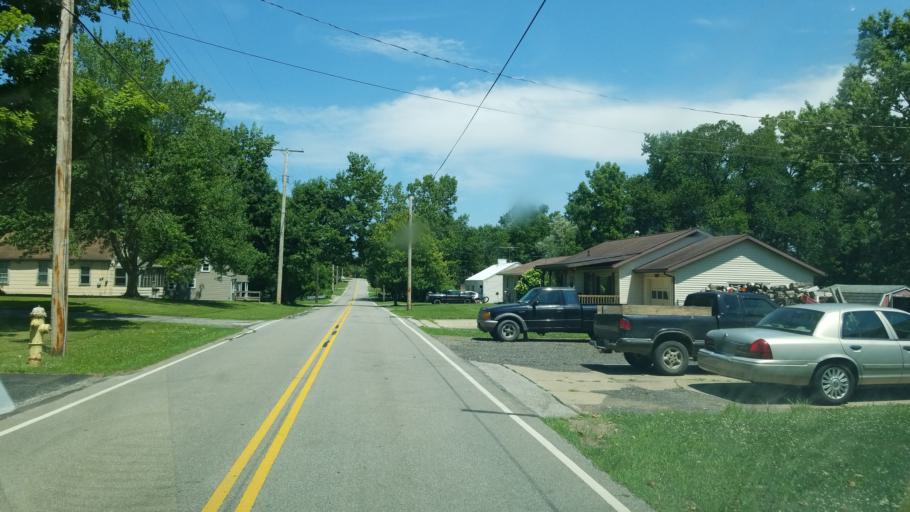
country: US
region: Ohio
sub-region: Ashland County
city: Ashland
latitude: 40.8674
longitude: -82.2987
